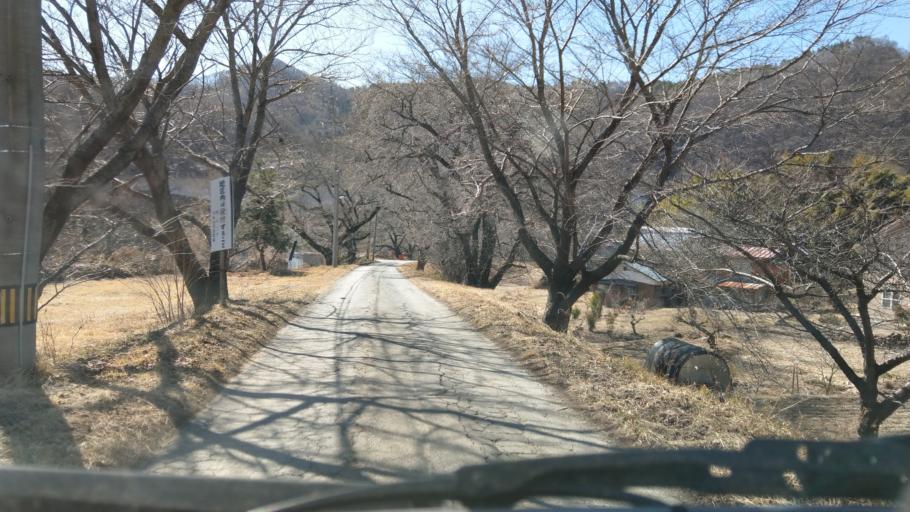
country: JP
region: Nagano
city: Komoro
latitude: 36.3324
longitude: 138.3946
